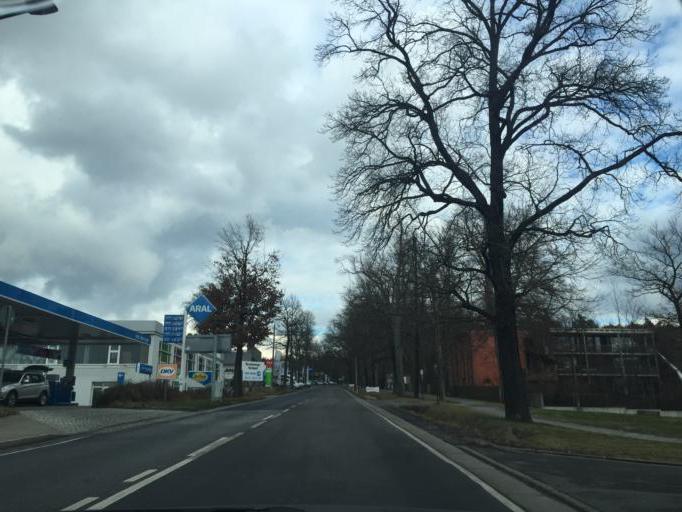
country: DE
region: Saxony
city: Albertstadt
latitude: 51.0703
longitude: 13.7886
